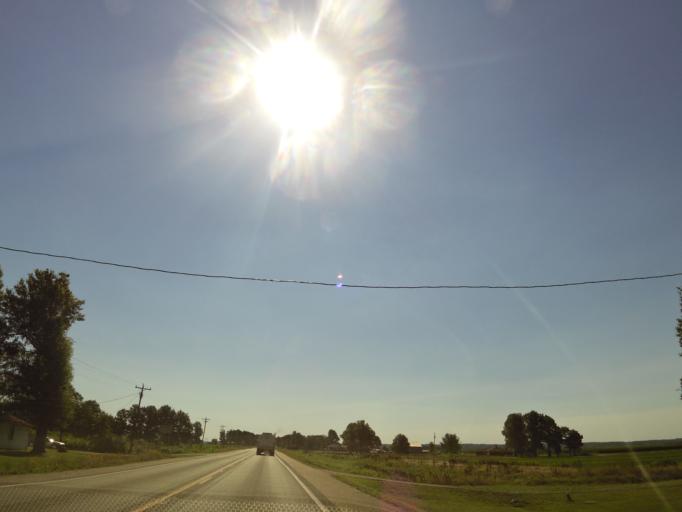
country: US
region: Arkansas
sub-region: Clay County
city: Corning
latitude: 36.4345
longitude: -90.3874
